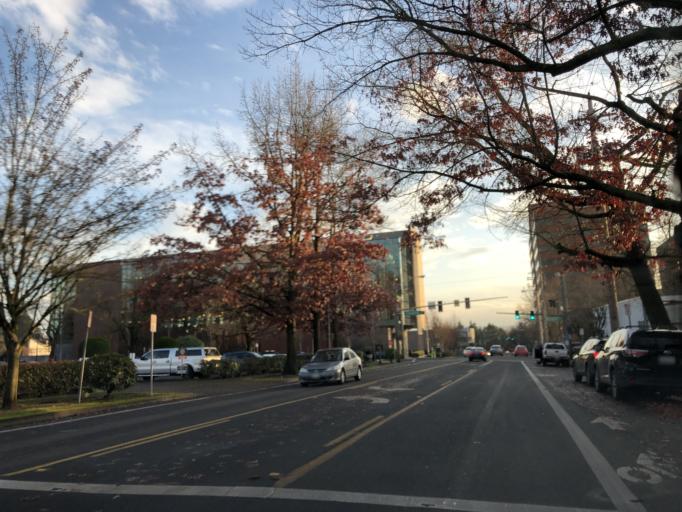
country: US
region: Washington
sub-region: Clark County
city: Vancouver
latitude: 45.6295
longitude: -122.6695
